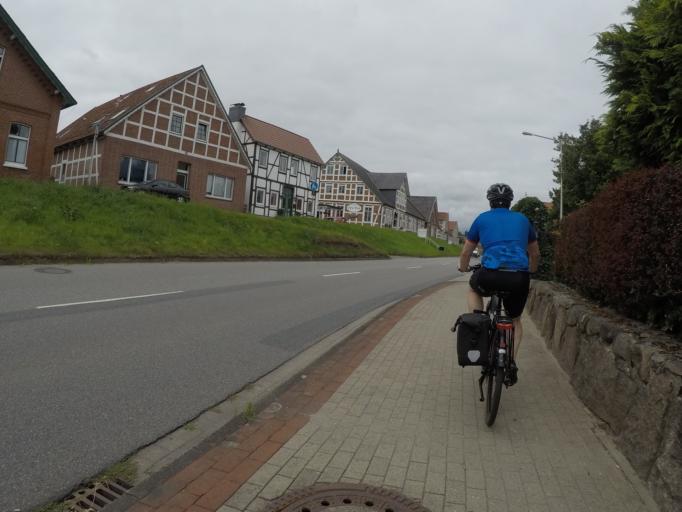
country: DE
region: Lower Saxony
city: Mittelnkirchen
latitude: 53.5427
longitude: 9.6170
